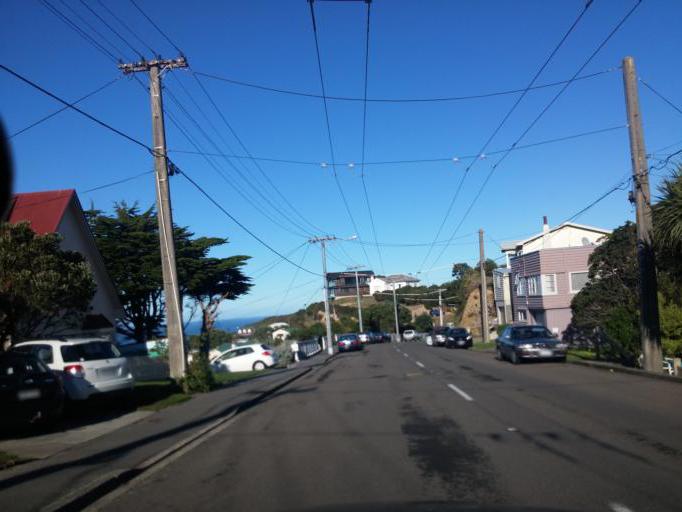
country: NZ
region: Wellington
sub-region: Wellington City
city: Brooklyn
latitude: -41.3198
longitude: 174.7642
